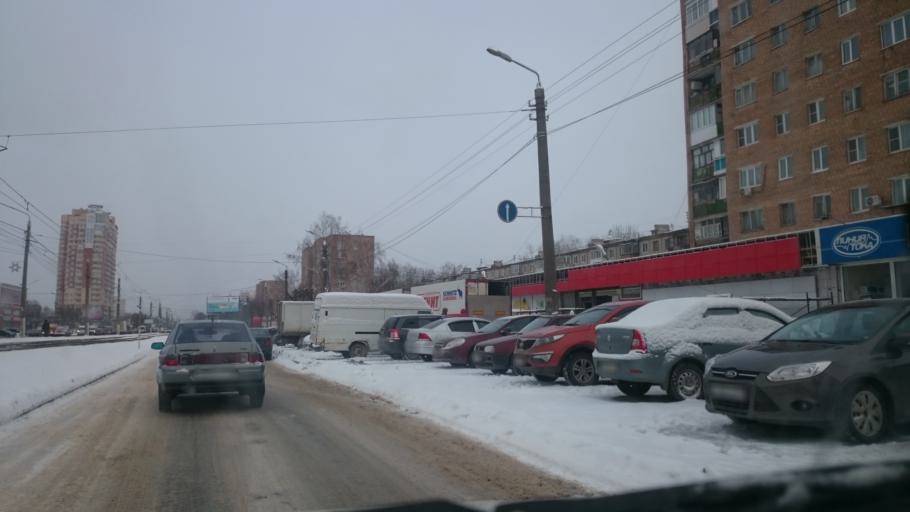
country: RU
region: Tula
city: Mendeleyevskiy
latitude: 54.1509
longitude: 37.5840
